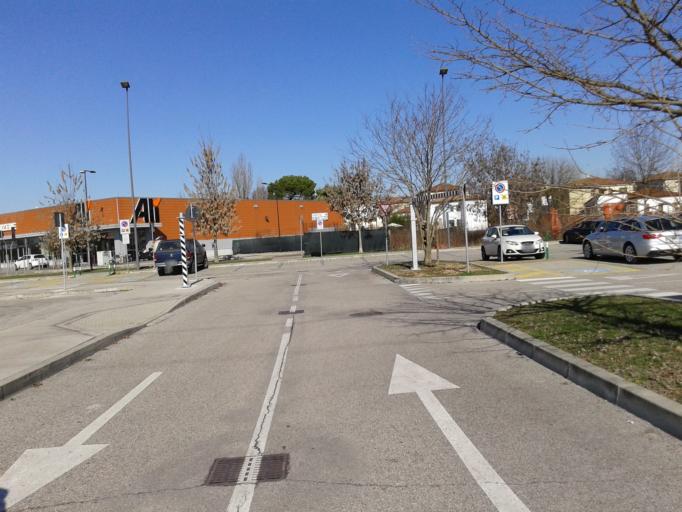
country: IT
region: Veneto
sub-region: Provincia di Padova
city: Vigodarzere
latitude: 45.4424
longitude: 11.8907
